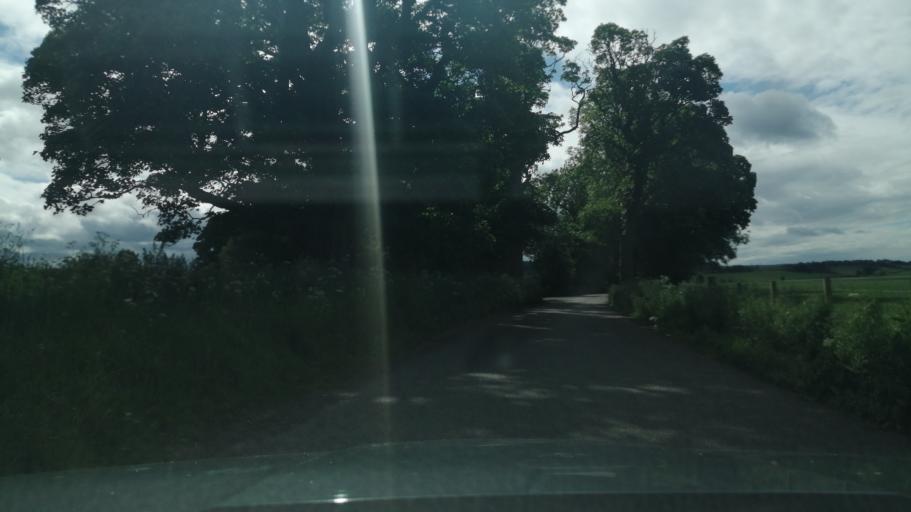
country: GB
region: Scotland
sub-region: Moray
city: Lhanbryd
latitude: 57.6555
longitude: -3.2563
